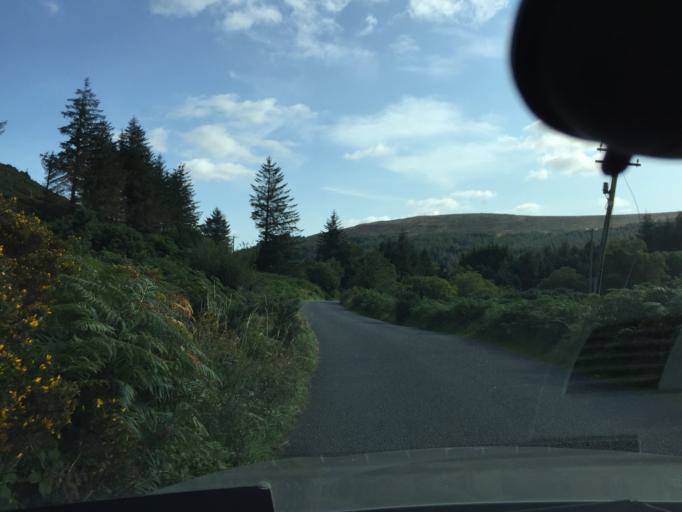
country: IE
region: Leinster
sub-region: Wicklow
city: Rathdrum
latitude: 53.0420
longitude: -6.3260
